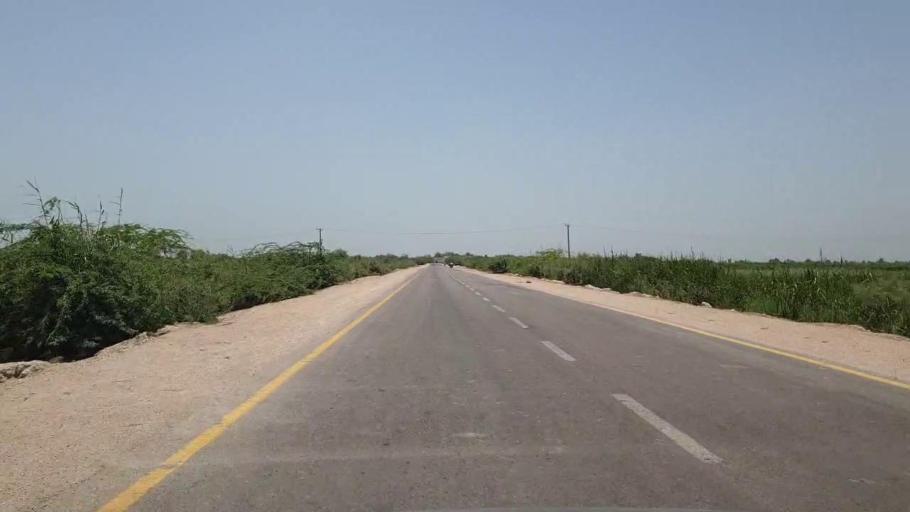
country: PK
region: Sindh
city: Sakrand
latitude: 26.1147
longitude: 68.3872
